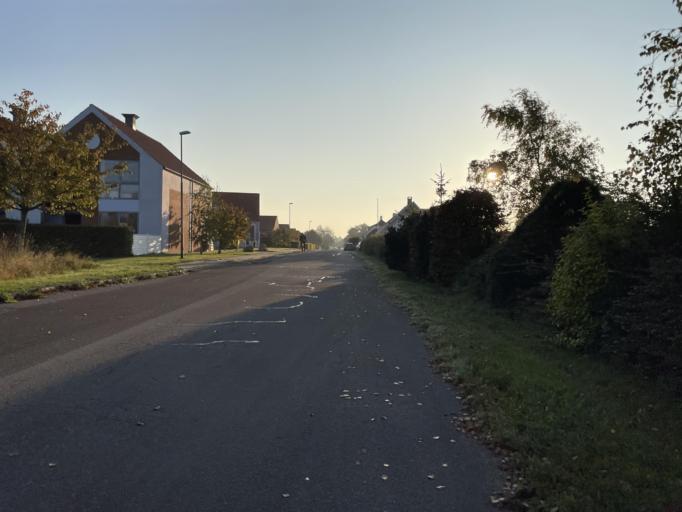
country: DK
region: South Denmark
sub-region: Kerteminde Kommune
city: Kerteminde
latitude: 55.4526
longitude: 10.6402
